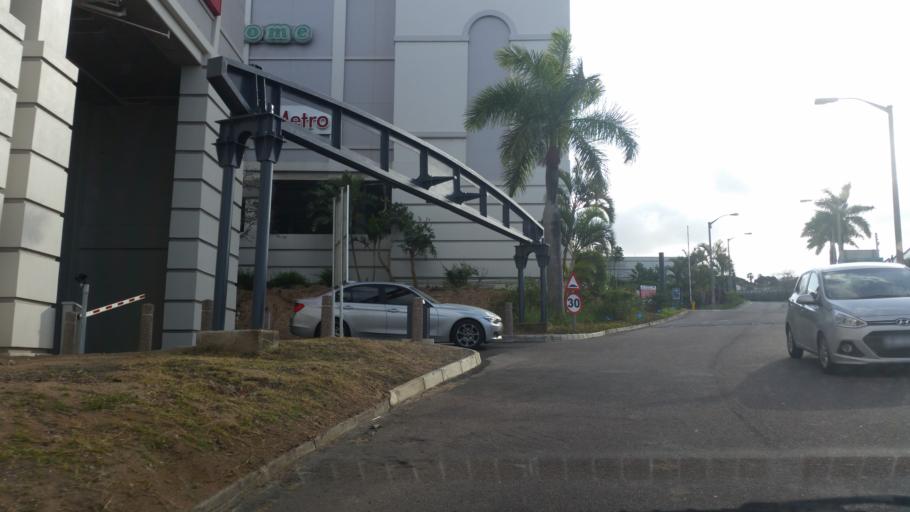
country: ZA
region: KwaZulu-Natal
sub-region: eThekwini Metropolitan Municipality
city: Berea
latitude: -29.8475
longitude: 30.9376
